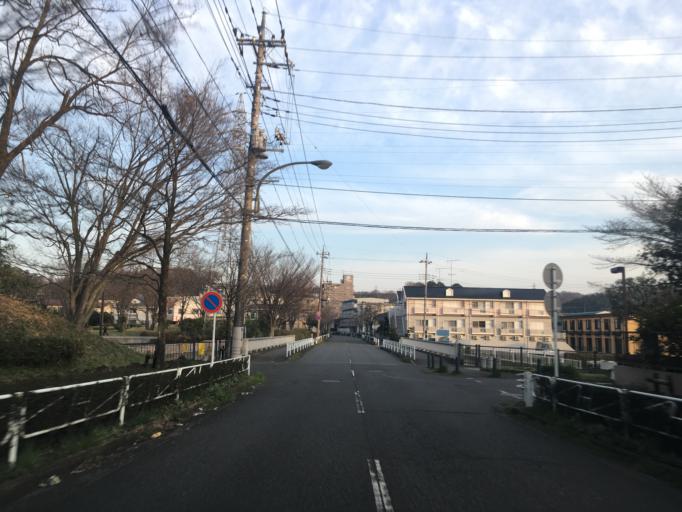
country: JP
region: Tokyo
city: Hino
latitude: 35.6303
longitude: 139.4069
